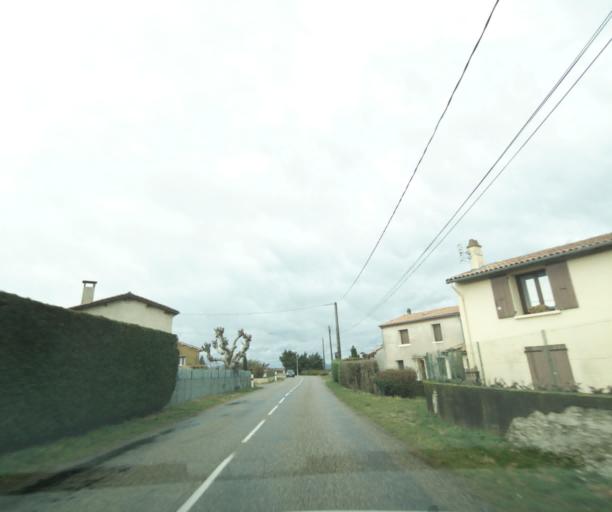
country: FR
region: Rhone-Alpes
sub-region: Departement de la Drome
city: Bourg-les-Valence
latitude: 44.9593
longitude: 4.9223
